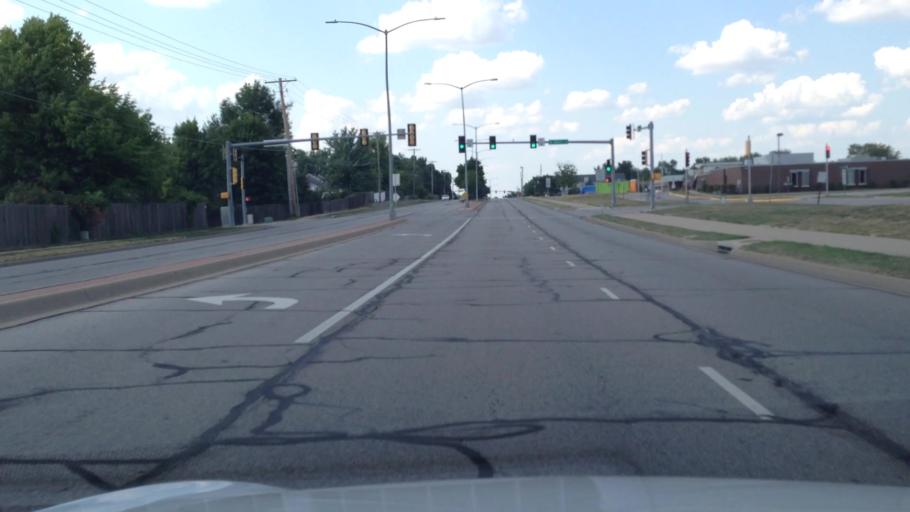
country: US
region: Kansas
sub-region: Johnson County
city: Olathe
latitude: 38.8998
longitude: -94.7973
